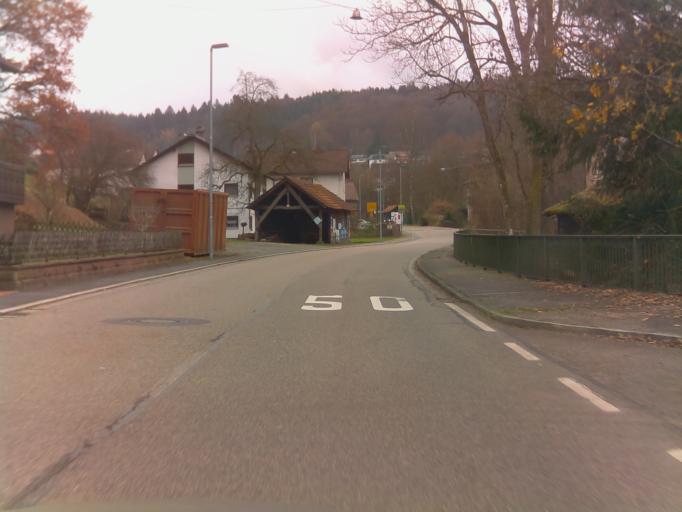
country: DE
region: Baden-Wuerttemberg
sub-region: Karlsruhe Region
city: Eberbach
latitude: 49.4296
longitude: 8.9573
